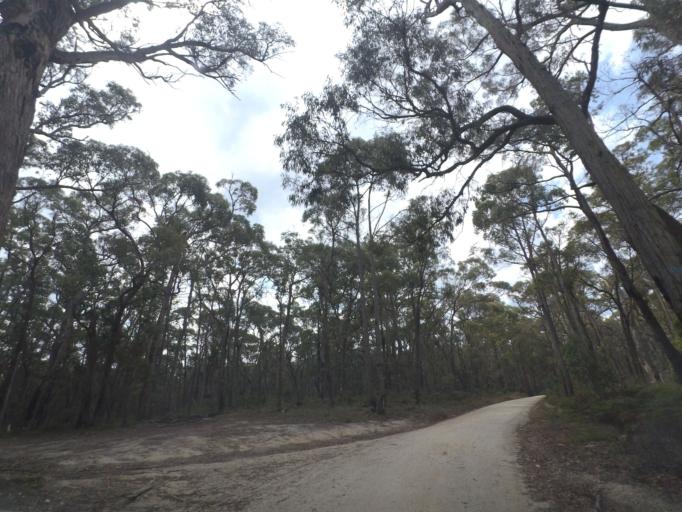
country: AU
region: Victoria
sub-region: Moorabool
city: Bacchus Marsh
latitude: -37.5072
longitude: 144.4276
